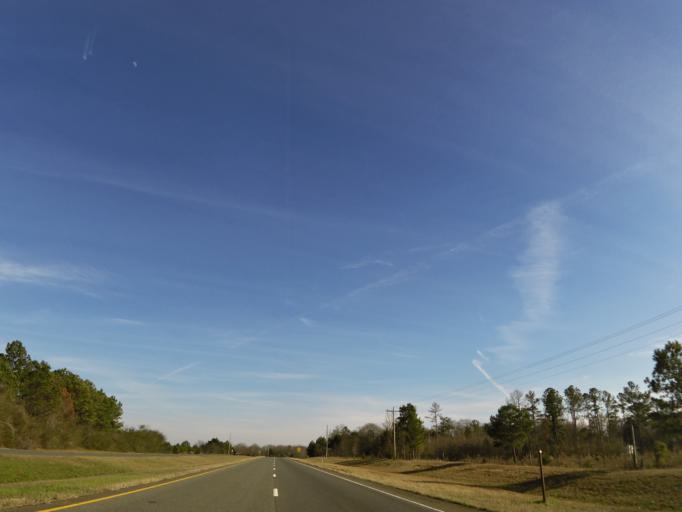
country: US
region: Georgia
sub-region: Stewart County
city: Richland
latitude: 32.1627
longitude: -84.7030
